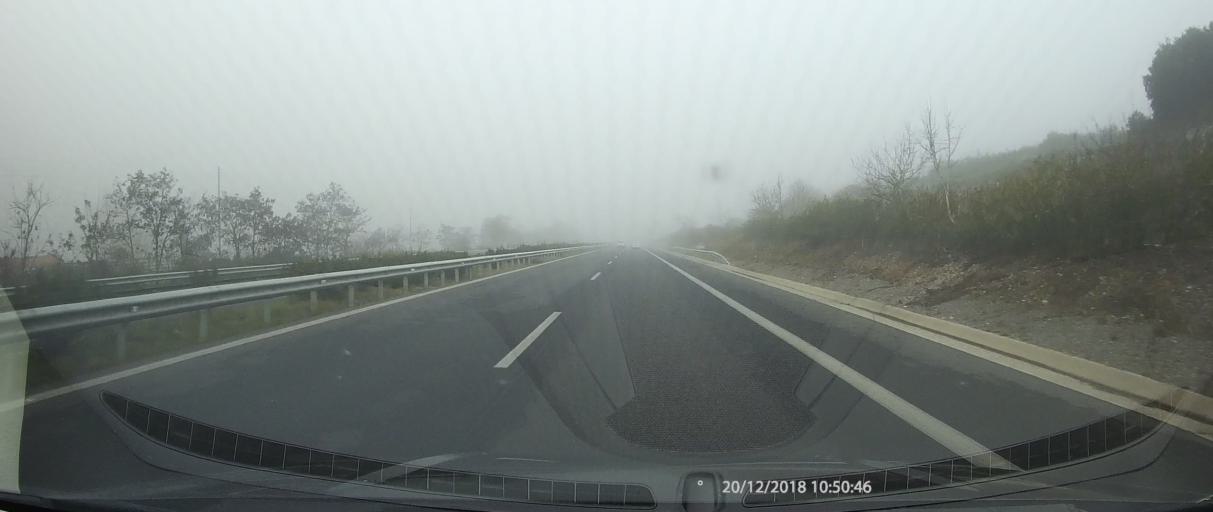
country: GR
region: Peloponnese
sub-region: Nomos Arkadias
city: Tripoli
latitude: 37.5704
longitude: 22.4277
